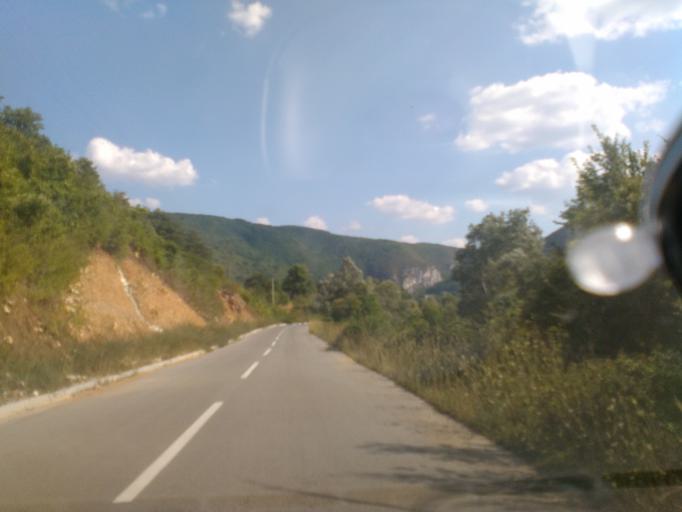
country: BA
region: Federation of Bosnia and Herzegovina
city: Orasac
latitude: 44.4988
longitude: 16.1327
